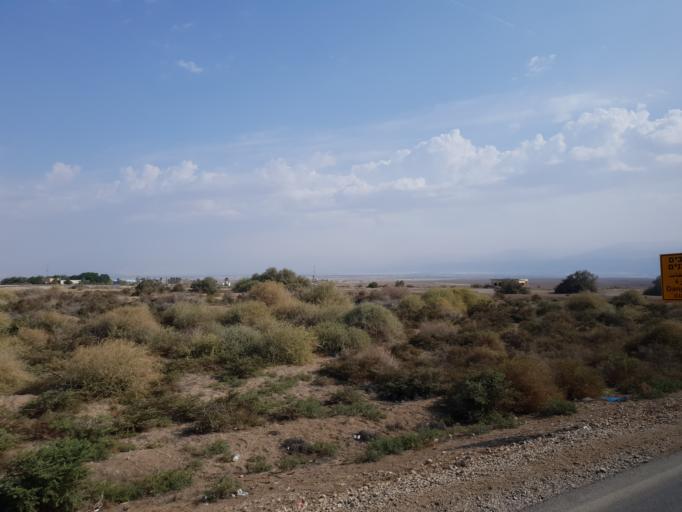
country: PS
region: West Bank
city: Jericho
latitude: 31.7702
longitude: 35.4989
